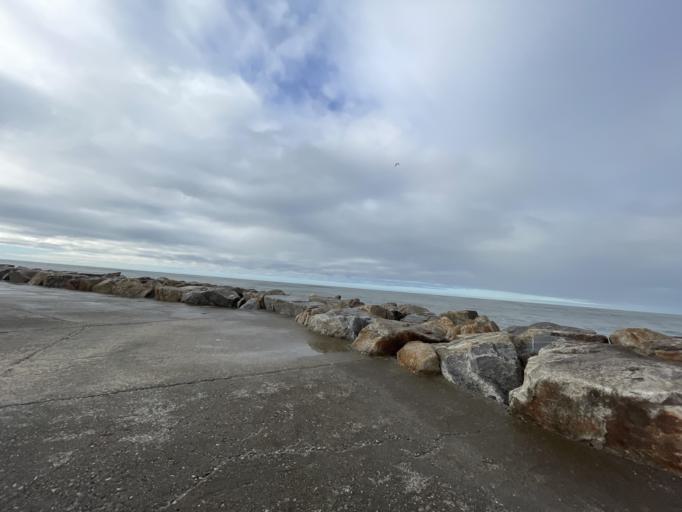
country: PT
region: Aveiro
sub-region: Espinho
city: Espinho
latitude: 41.0093
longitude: -8.6486
